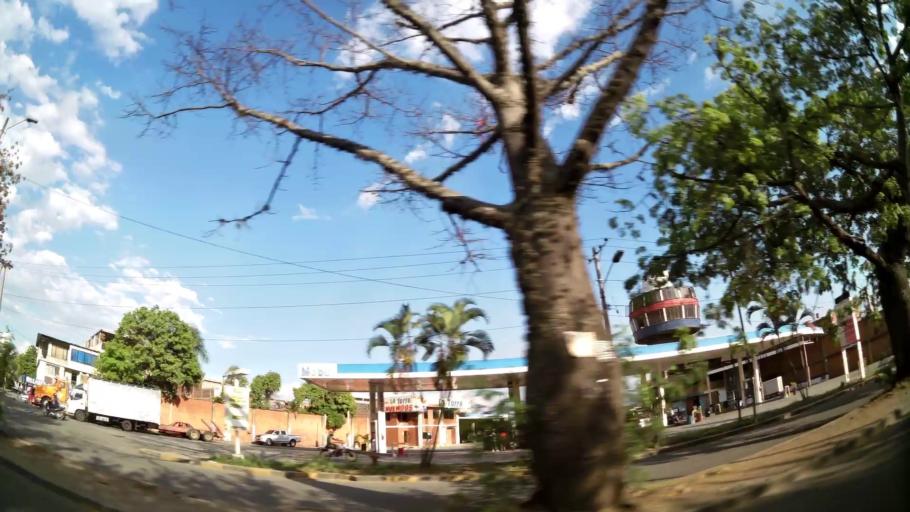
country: CO
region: Valle del Cauca
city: Cali
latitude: 3.4335
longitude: -76.4960
